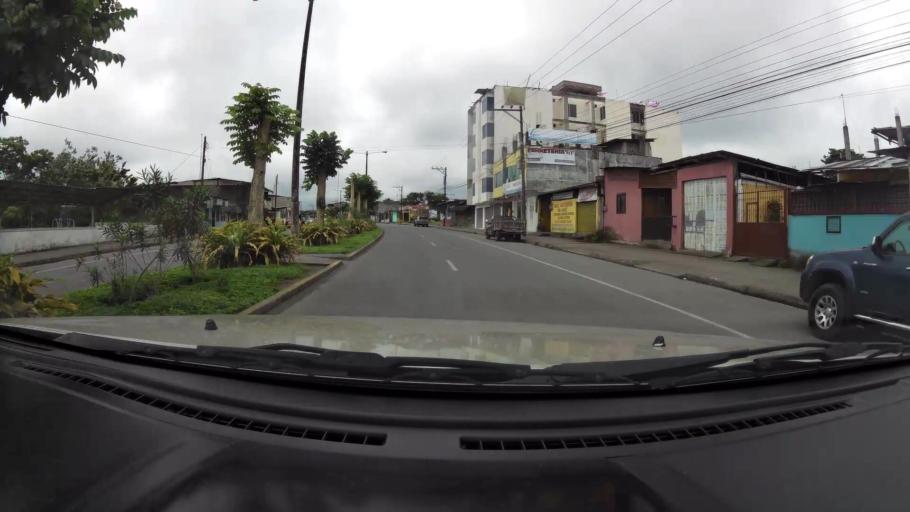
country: EC
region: Santo Domingo de los Tsachilas
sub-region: Canton Santo Domingo de los Colorados
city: Santo Domingo de los Colorados
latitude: -0.2658
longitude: -79.1763
